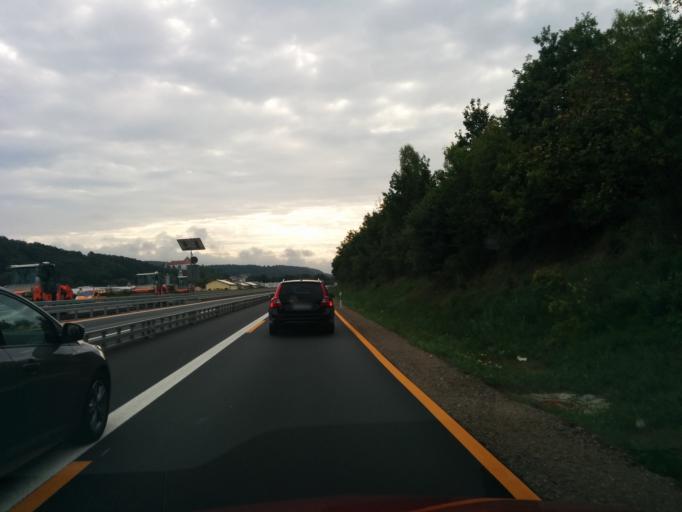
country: DE
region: Bavaria
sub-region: Upper Palatinate
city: Wiesent
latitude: 48.9996
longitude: 12.3809
